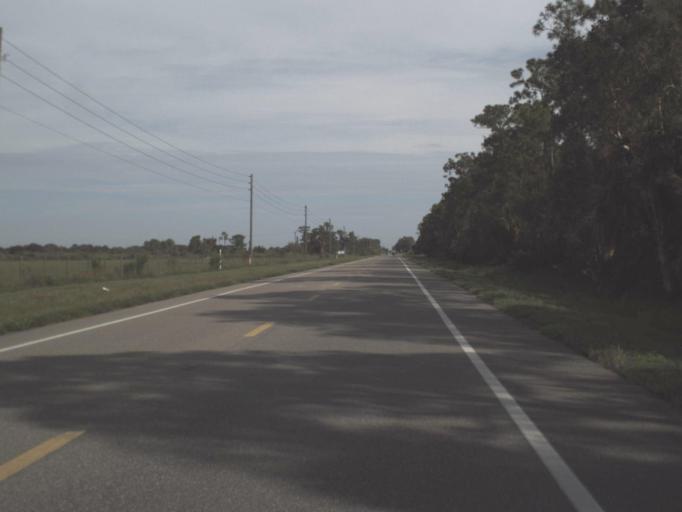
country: US
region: Florida
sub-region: DeSoto County
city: Nocatee
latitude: 27.0007
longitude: -81.7604
